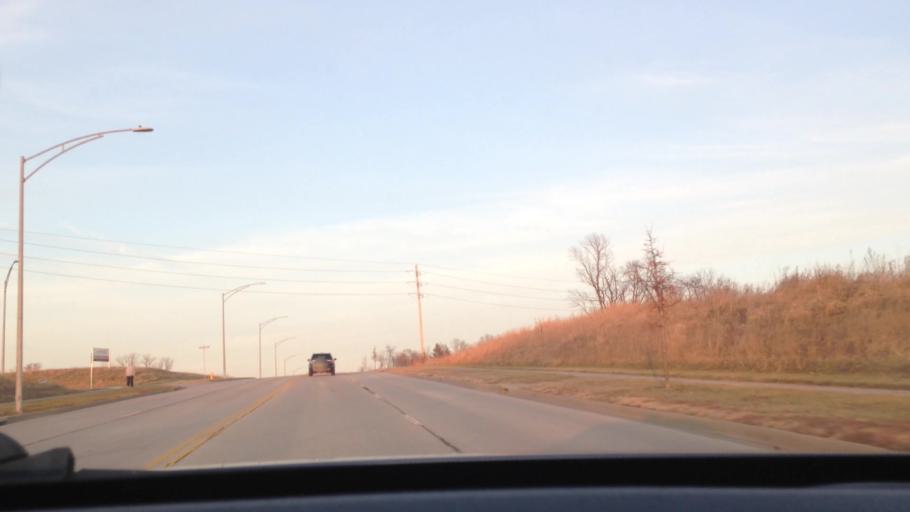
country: US
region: Missouri
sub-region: Clay County
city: Liberty
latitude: 39.2153
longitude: -94.4406
